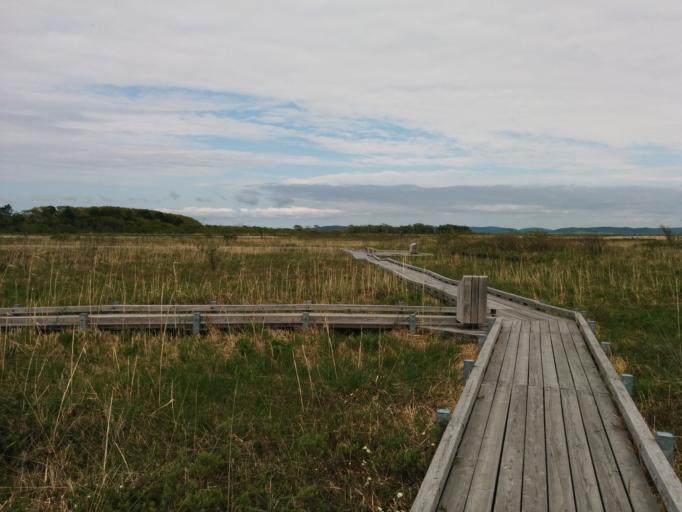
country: JP
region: Hokkaido
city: Makubetsu
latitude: 45.1082
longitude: 141.7027
